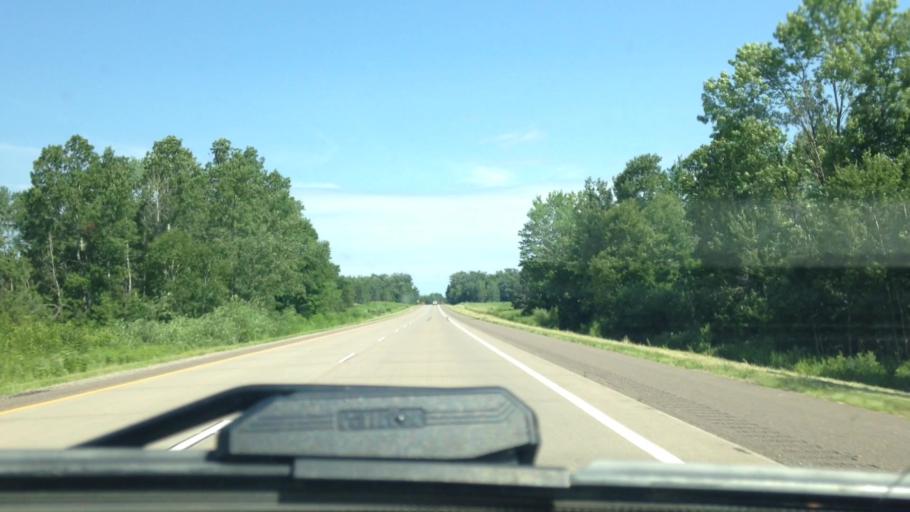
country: US
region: Wisconsin
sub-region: Barron County
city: Rice Lake
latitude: 45.5466
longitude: -91.7629
